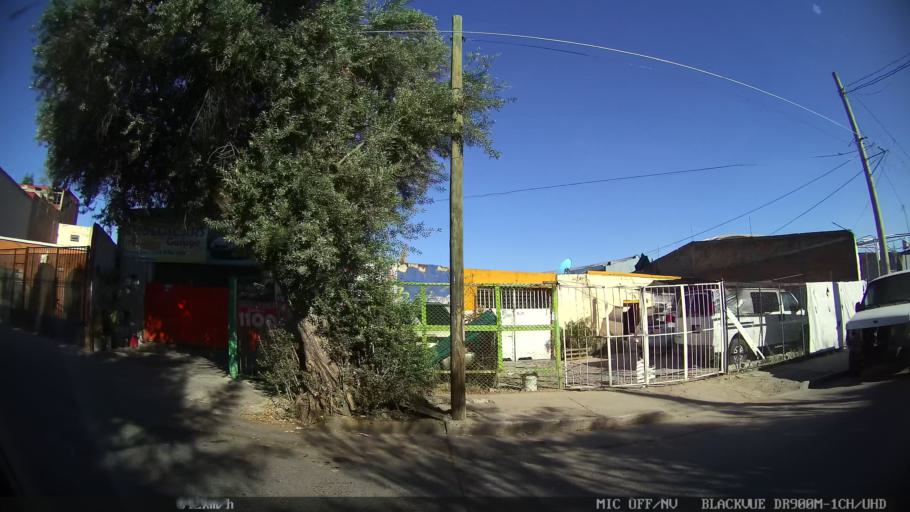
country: MX
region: Jalisco
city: Tlaquepaque
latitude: 20.6854
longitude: -103.3233
